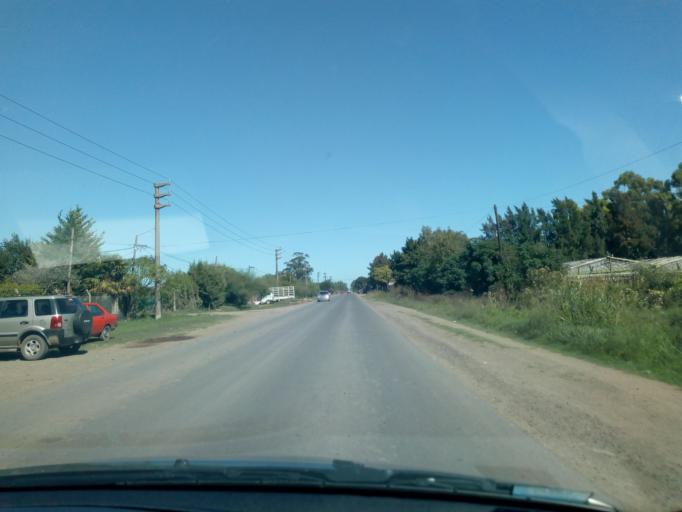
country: AR
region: Buenos Aires
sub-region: Partido de La Plata
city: La Plata
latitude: -35.0084
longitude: -58.0253
